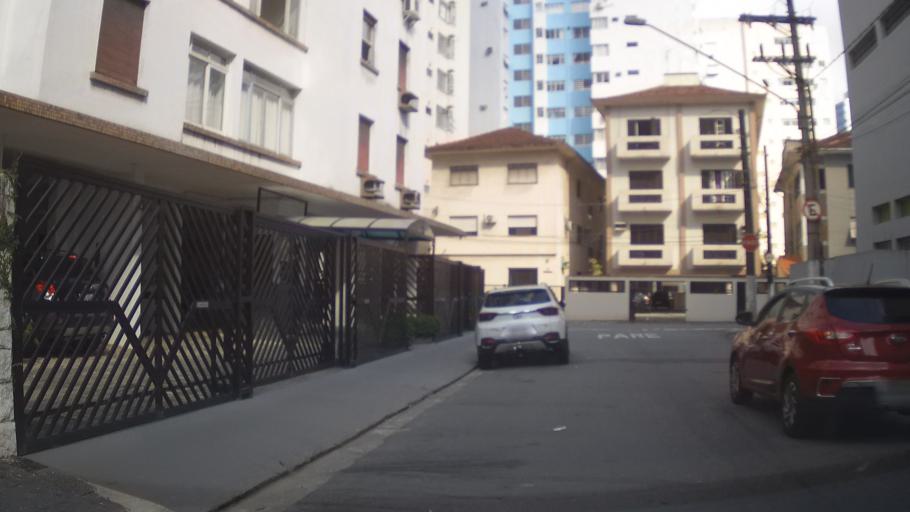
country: BR
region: Sao Paulo
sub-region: Santos
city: Santos
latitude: -23.9696
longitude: -46.3249
